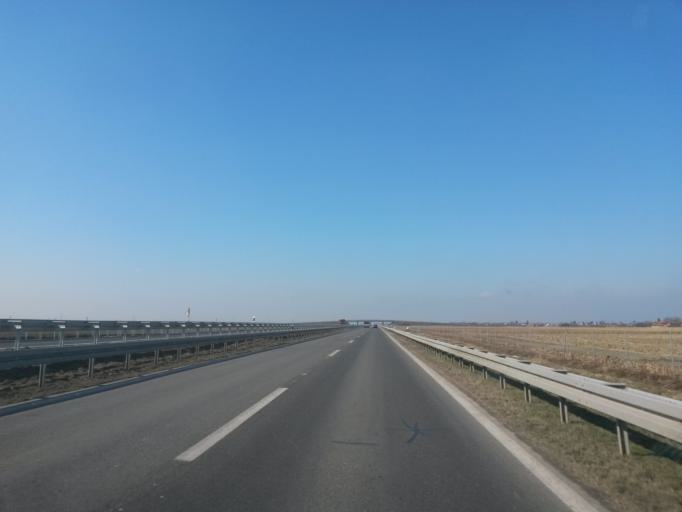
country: HR
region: Osjecko-Baranjska
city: Visnjevac
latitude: 45.5611
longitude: 18.5995
